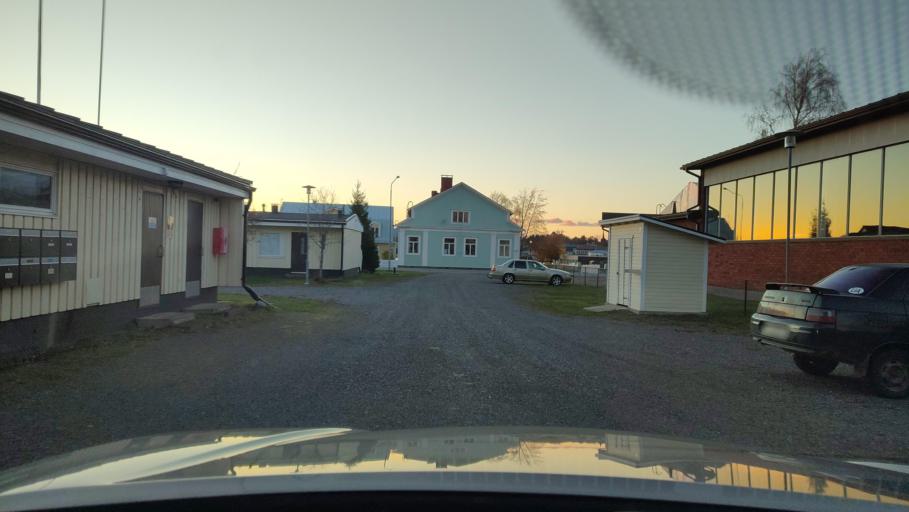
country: FI
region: Ostrobothnia
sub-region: Sydosterbotten
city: Kristinestad
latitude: 62.2718
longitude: 21.3889
